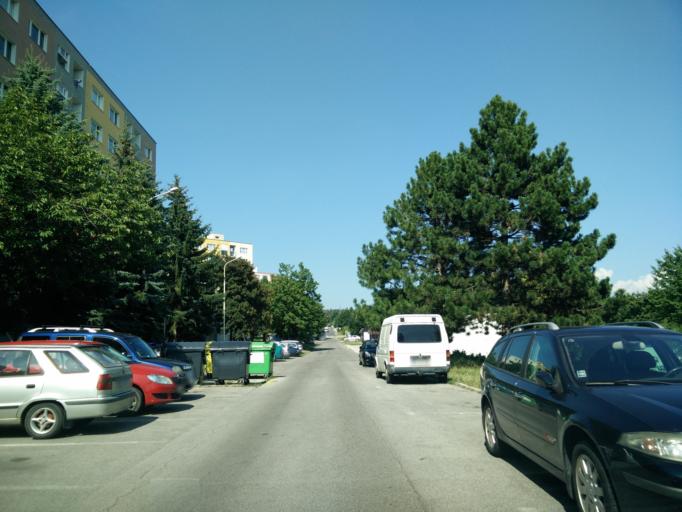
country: SK
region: Nitriansky
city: Prievidza
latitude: 48.7765
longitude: 18.6444
